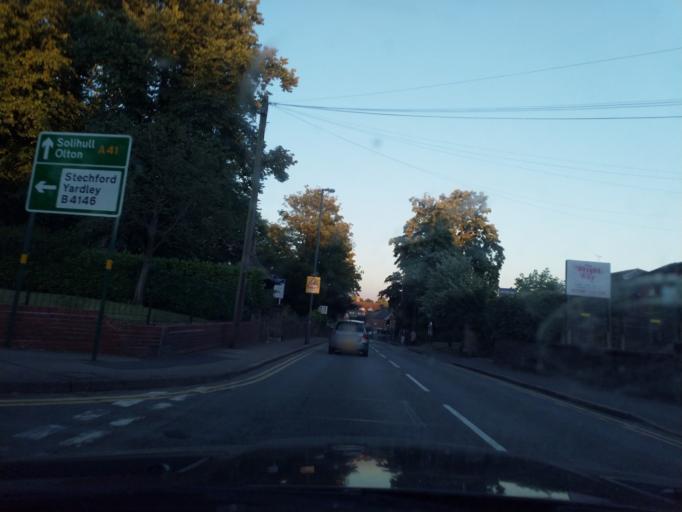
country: GB
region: England
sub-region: City and Borough of Birmingham
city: Acocks Green
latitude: 52.4478
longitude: -1.8260
